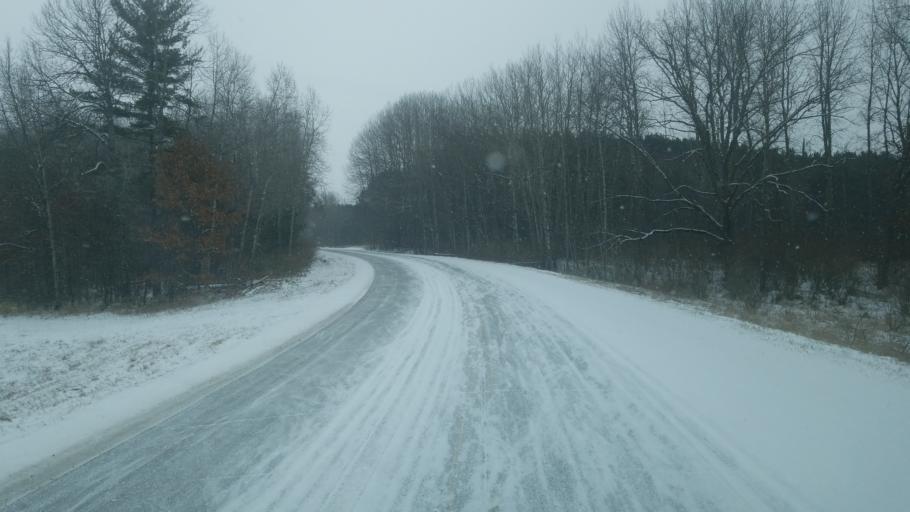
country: US
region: Michigan
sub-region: Mecosta County
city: Big Rapids
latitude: 43.7377
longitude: -85.4037
